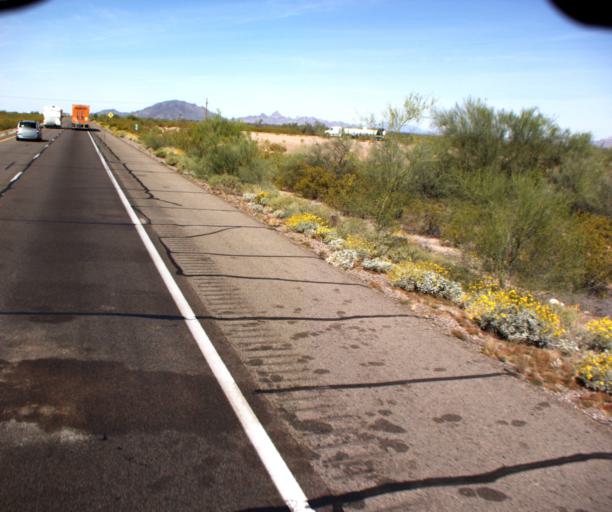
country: US
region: Arizona
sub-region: Maricopa County
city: Buckeye
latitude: 33.4979
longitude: -112.9386
